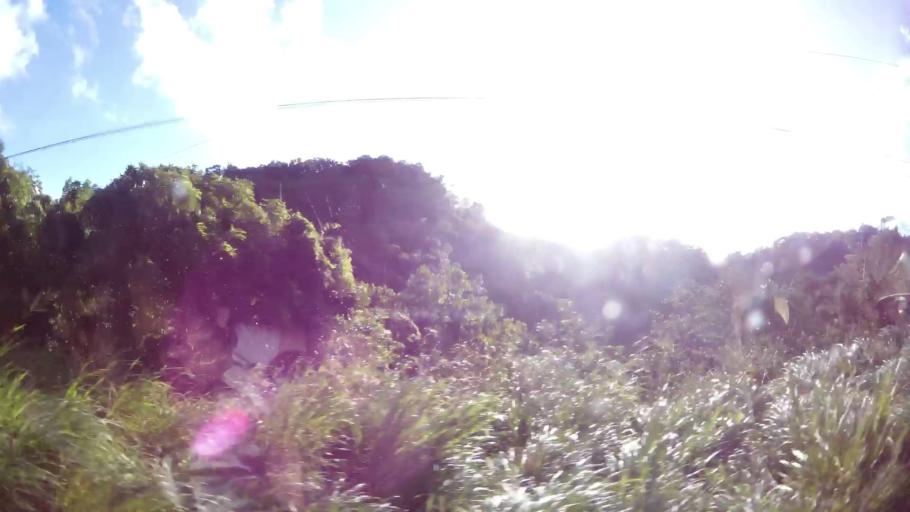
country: DM
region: Saint John
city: Portsmouth
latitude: 15.5828
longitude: -61.4149
